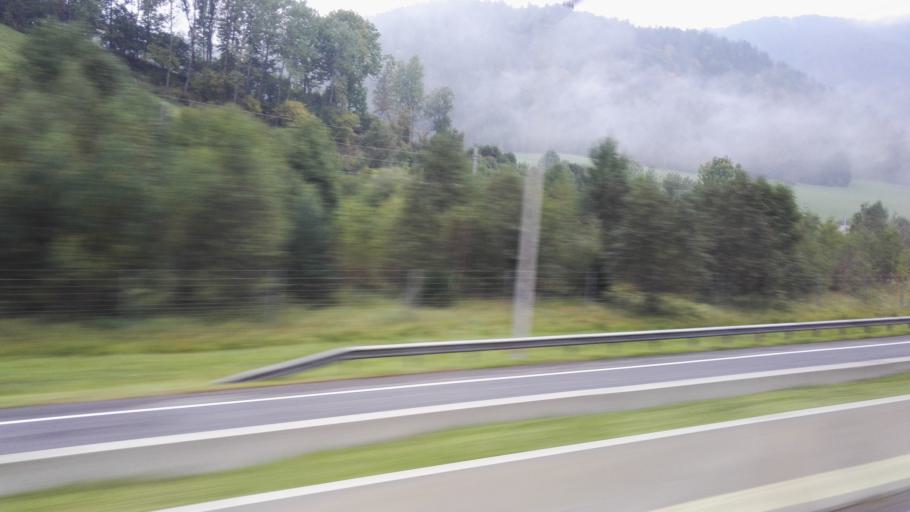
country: AT
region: Styria
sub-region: Politischer Bezirk Bruck-Muerzzuschlag
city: Spital am Semmering
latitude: 47.6100
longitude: 15.7397
